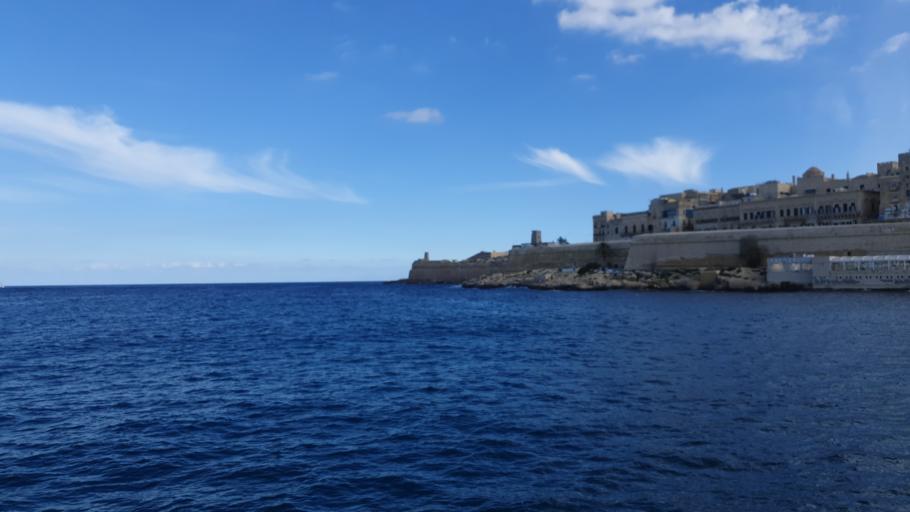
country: MT
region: Il-Belt Valletta
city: Valletta
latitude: 35.9023
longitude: 14.5095
